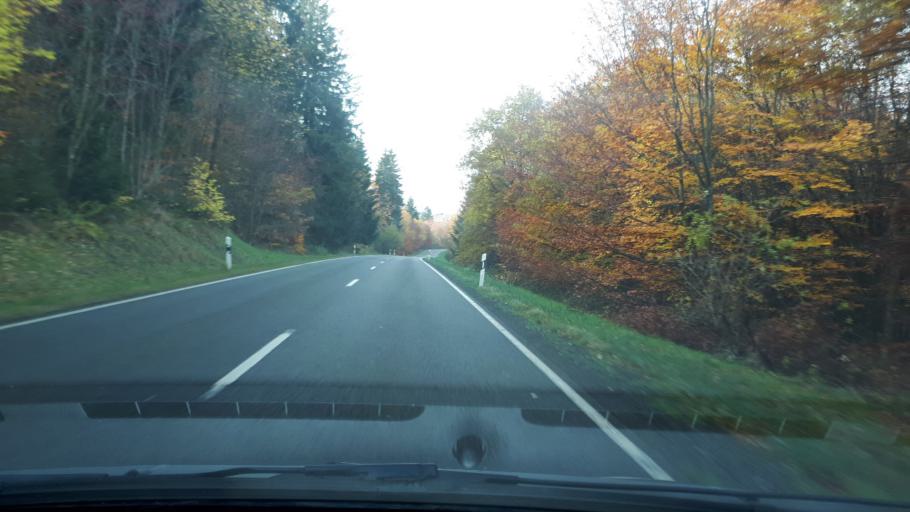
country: DE
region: Rheinland-Pfalz
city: Leienkaul
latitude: 50.2244
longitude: 7.0954
